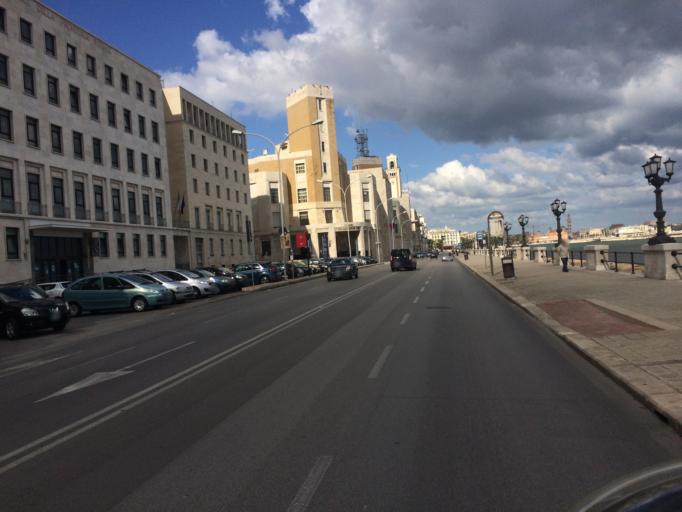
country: IT
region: Apulia
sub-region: Provincia di Bari
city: Bari
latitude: 41.1204
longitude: 16.8856
